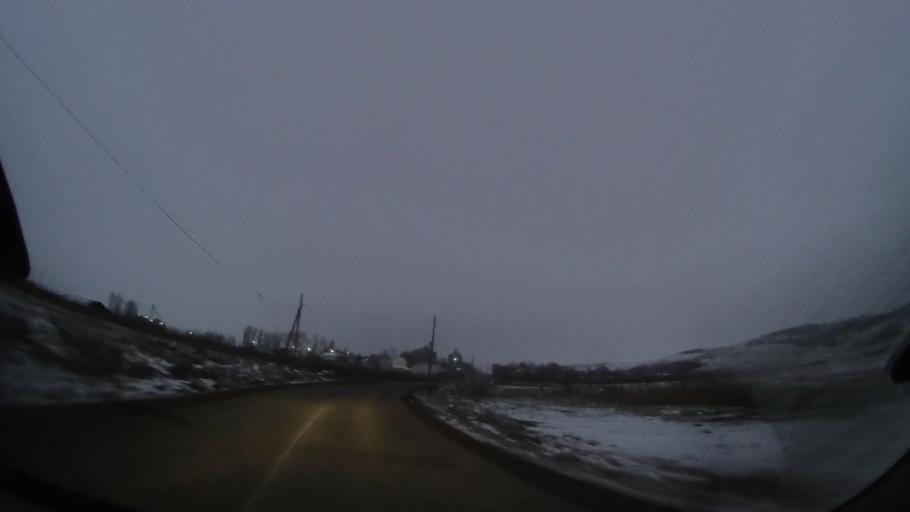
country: RO
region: Vaslui
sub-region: Comuna Dimitrie Cantemir
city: Dimitrie Cantemir
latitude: 46.4967
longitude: 28.0523
